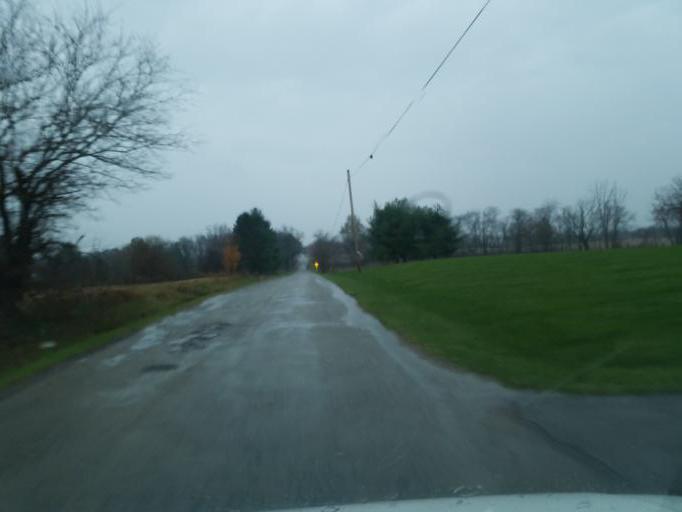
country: US
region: Ohio
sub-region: Morrow County
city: Cardington
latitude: 40.4623
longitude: -82.8953
